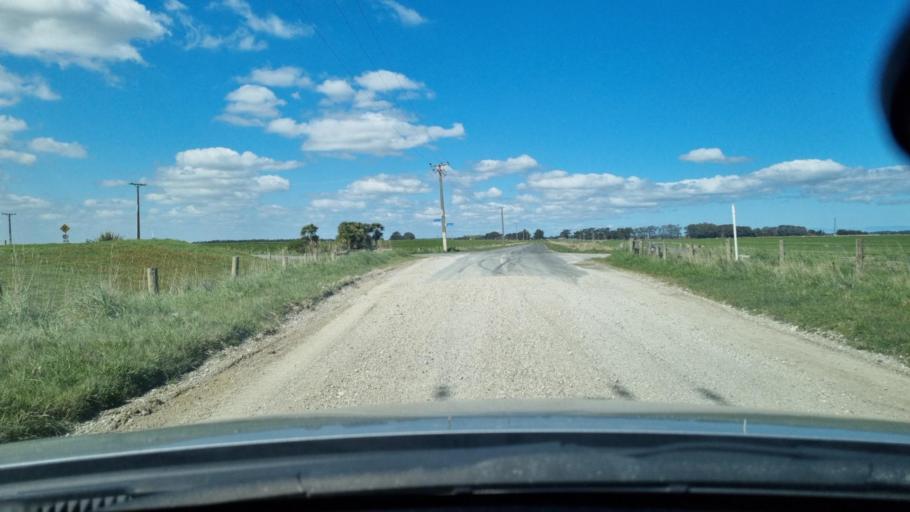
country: NZ
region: Southland
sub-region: Invercargill City
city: Invercargill
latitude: -46.3922
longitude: 168.2725
